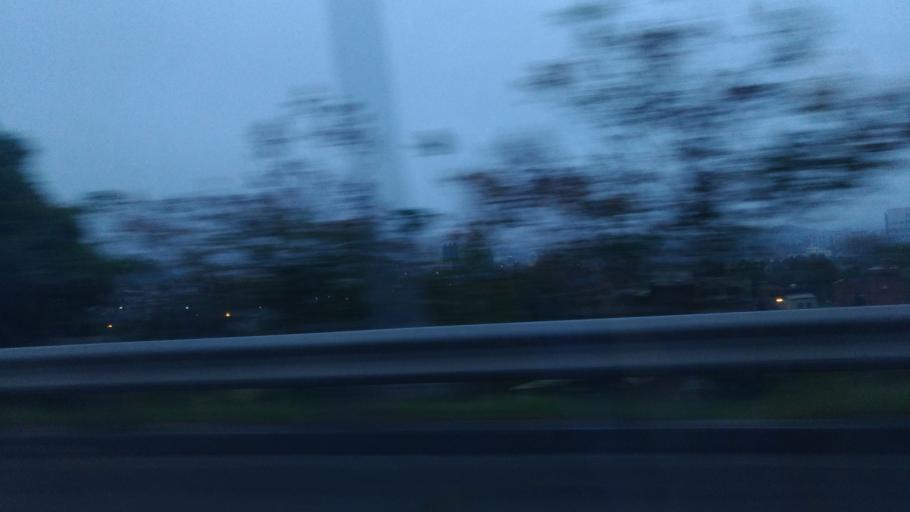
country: TW
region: Taiwan
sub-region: Hsinchu
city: Hsinchu
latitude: 24.7344
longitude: 120.9087
